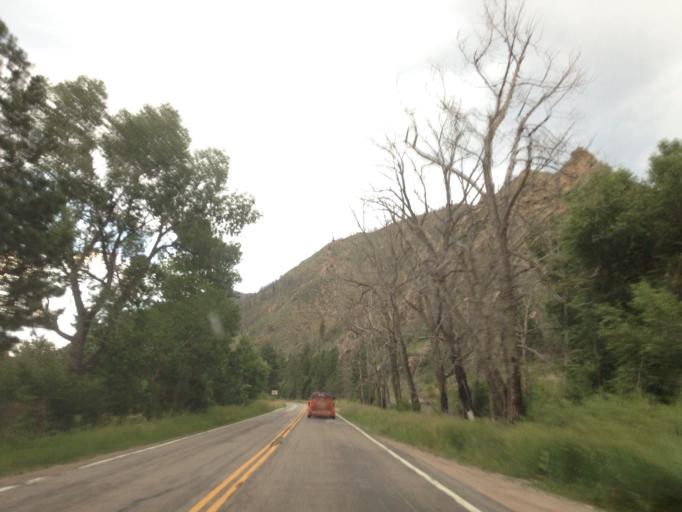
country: US
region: Colorado
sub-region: Larimer County
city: Laporte
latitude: 40.6828
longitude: -105.4083
